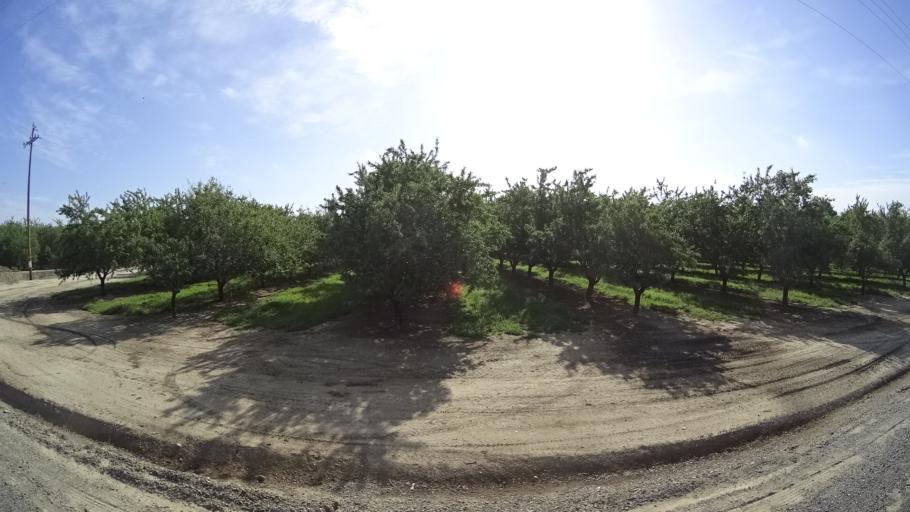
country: US
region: California
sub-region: Glenn County
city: Hamilton City
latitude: 39.6073
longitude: -122.0076
